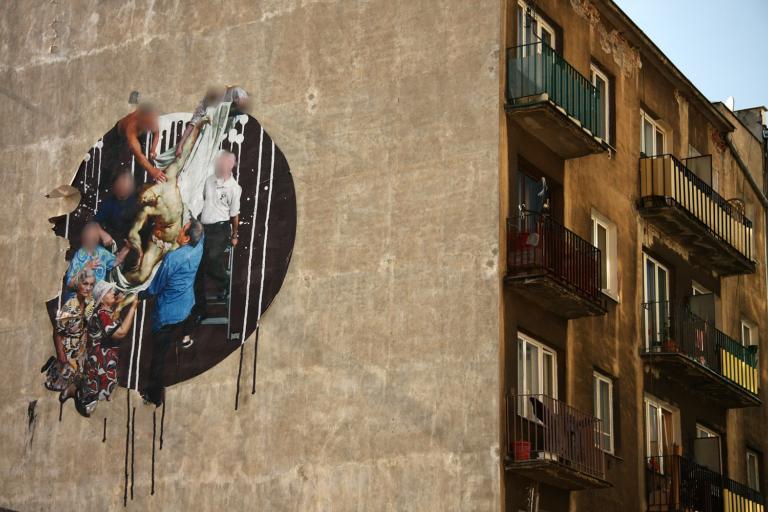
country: PL
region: Masovian Voivodeship
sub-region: Warszawa
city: Praga Polnoc
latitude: 52.2530
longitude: 21.0415
